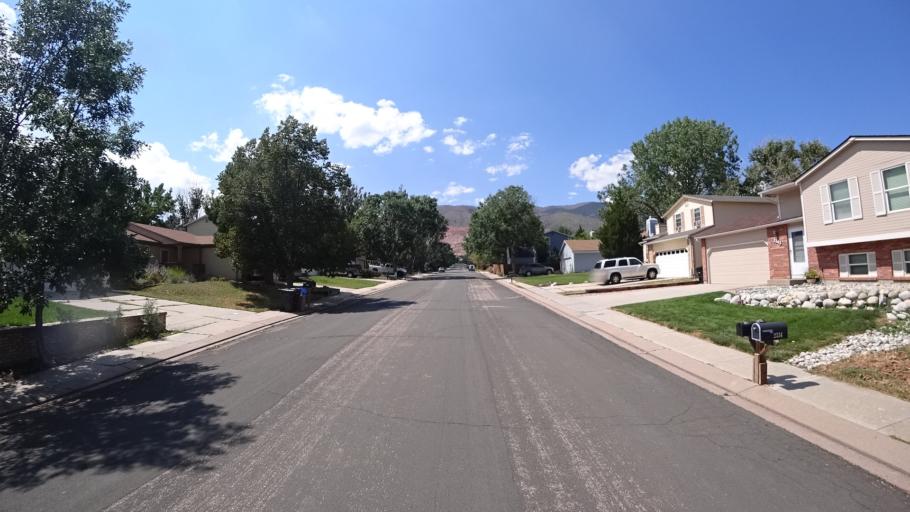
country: US
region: Colorado
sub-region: El Paso County
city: Air Force Academy
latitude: 38.9353
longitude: -104.8706
